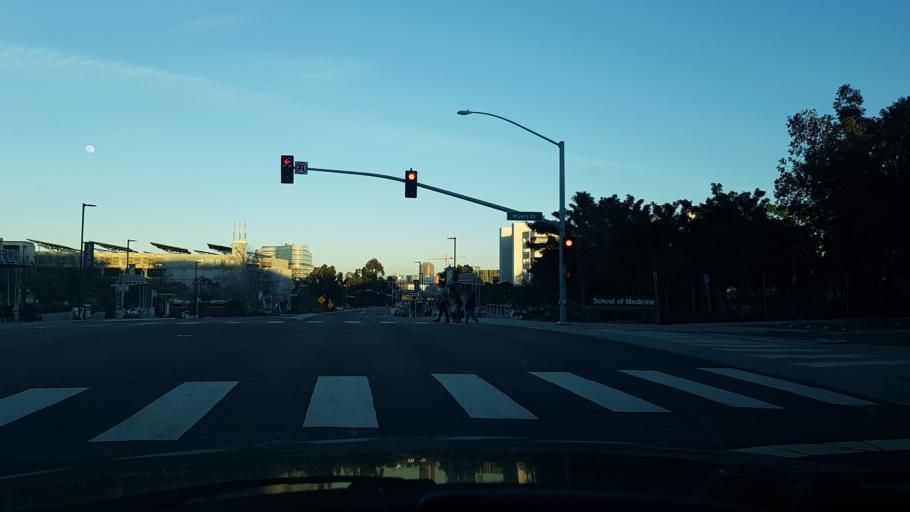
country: US
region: California
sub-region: San Diego County
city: La Jolla
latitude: 32.8770
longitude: -117.2362
